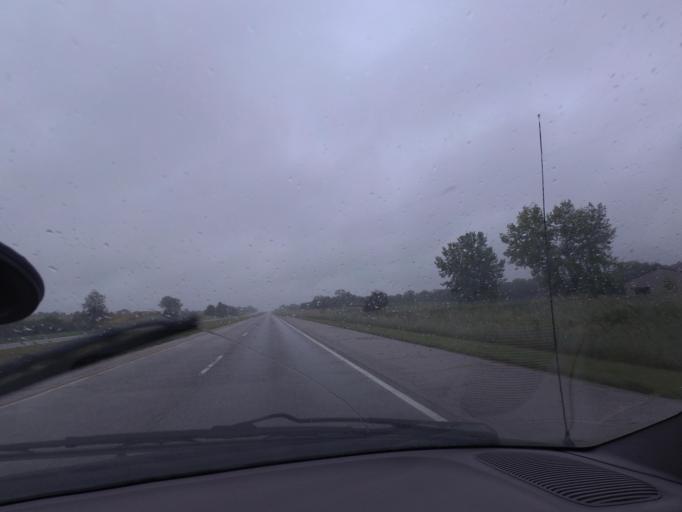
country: US
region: Illinois
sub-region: Pike County
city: Barry
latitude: 39.6890
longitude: -90.9108
